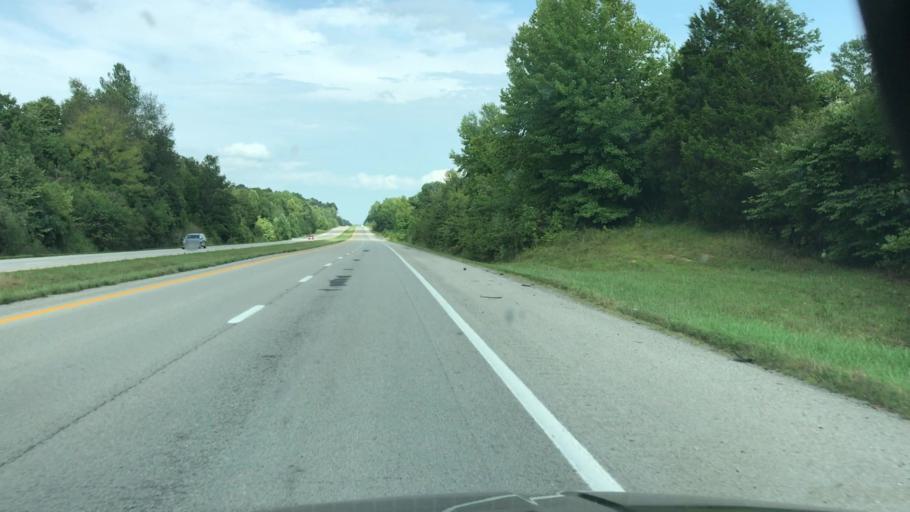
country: US
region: Kentucky
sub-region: Hopkins County
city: Nortonville
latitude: 37.2034
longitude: -87.5184
